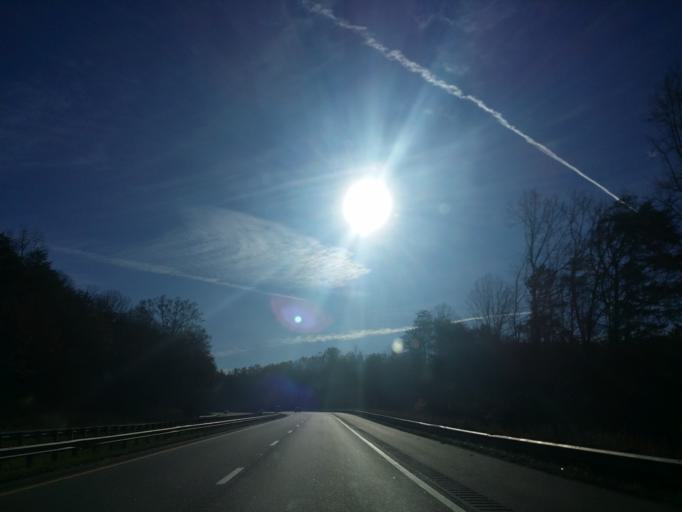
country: US
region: North Carolina
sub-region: McDowell County
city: West Marion
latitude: 35.6382
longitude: -82.1096
